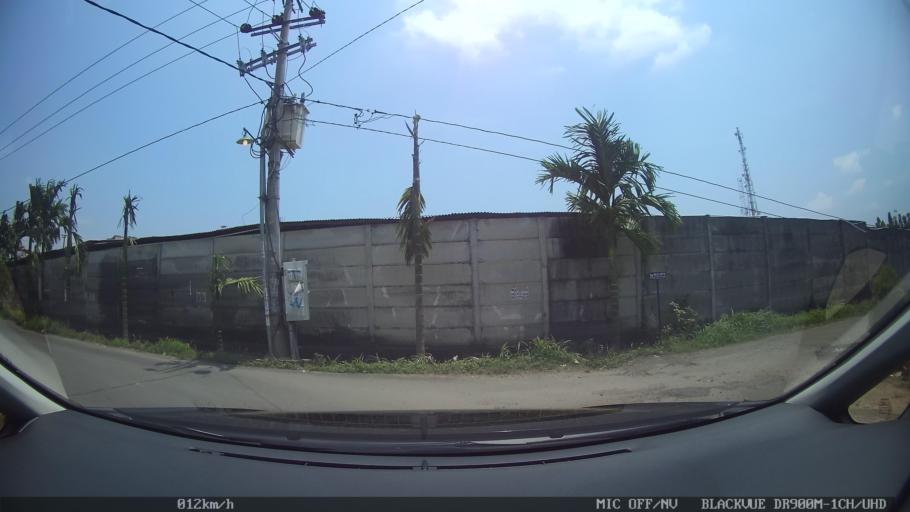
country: ID
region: Lampung
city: Kedaton
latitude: -5.3662
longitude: 105.2572
